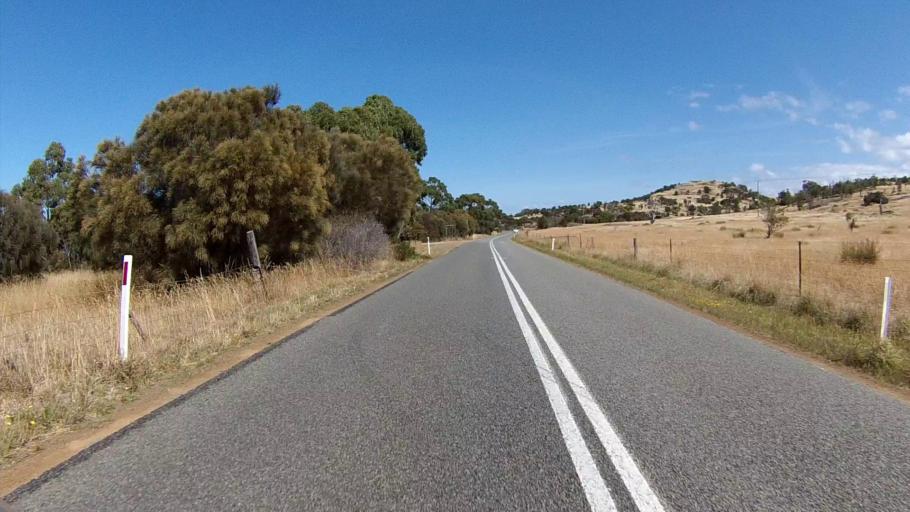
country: AU
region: Tasmania
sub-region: Sorell
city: Sorell
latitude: -42.1840
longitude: 148.0670
